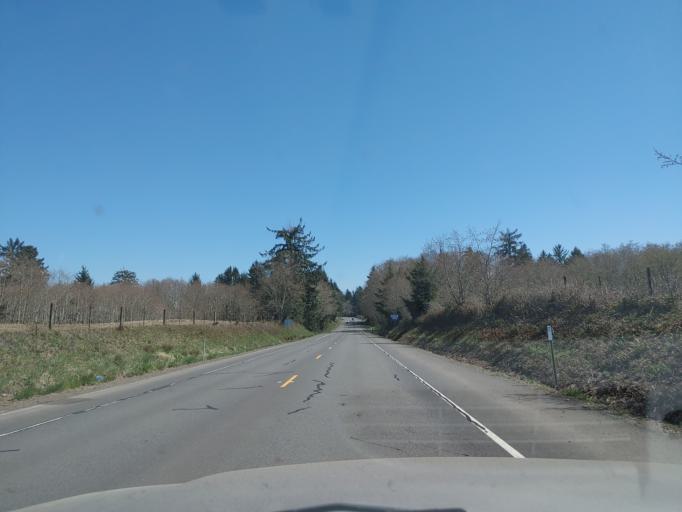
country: US
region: Oregon
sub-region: Clatsop County
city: Warrenton
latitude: 46.1433
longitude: -123.8806
